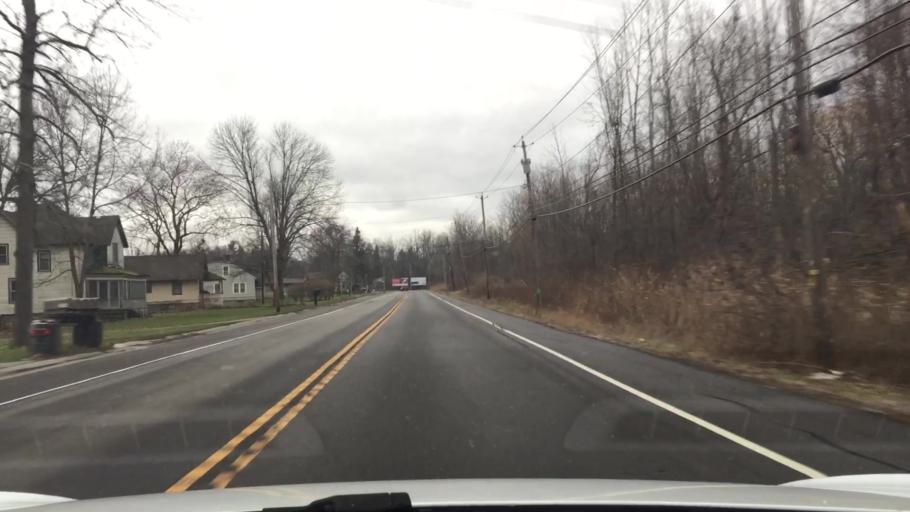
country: US
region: New York
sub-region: Erie County
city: Tonawanda
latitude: 43.0674
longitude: -78.9247
